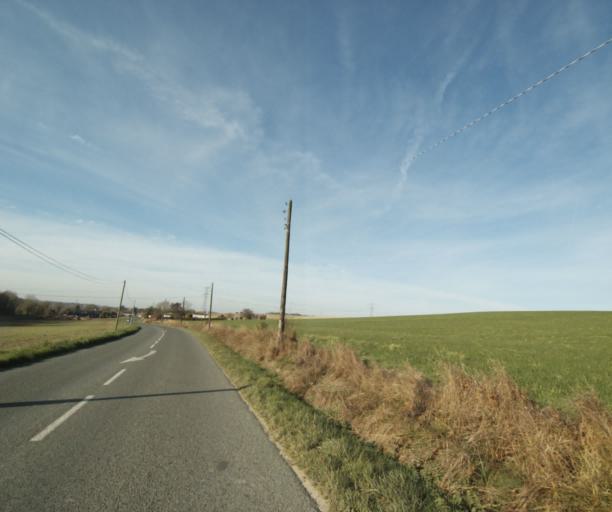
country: FR
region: Poitou-Charentes
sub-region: Departement de la Charente-Maritime
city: Chaniers
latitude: 45.7254
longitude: -0.5744
